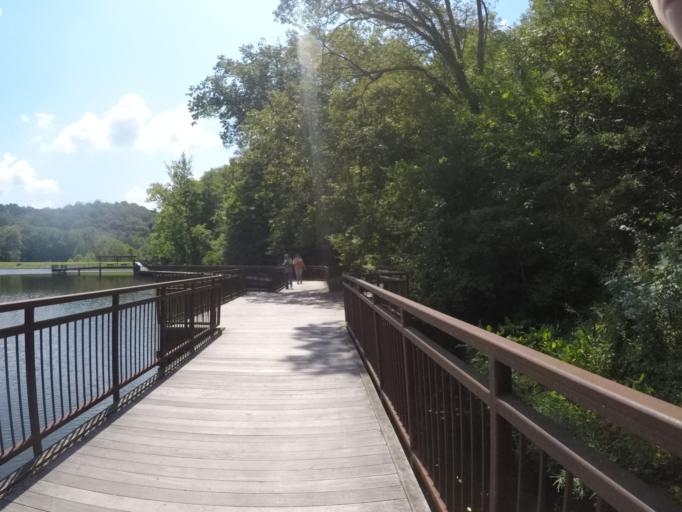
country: US
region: Ohio
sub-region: Lawrence County
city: Ironton
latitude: 38.6076
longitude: -82.6334
